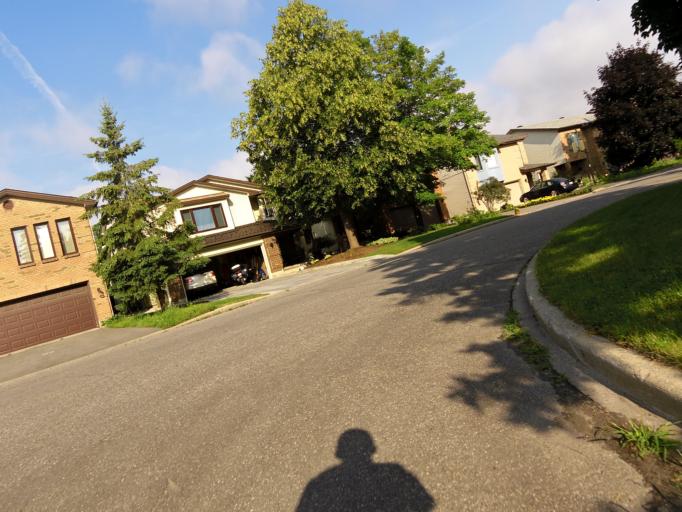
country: CA
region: Ontario
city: Ottawa
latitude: 45.3446
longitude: -75.6890
